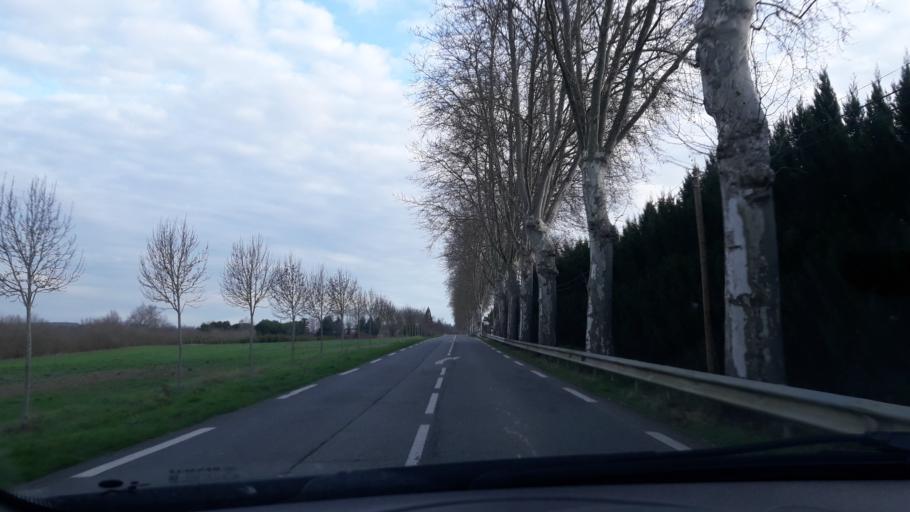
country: FR
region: Midi-Pyrenees
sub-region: Departement de la Haute-Garonne
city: Montaigut-sur-Save
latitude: 43.6973
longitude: 1.2368
